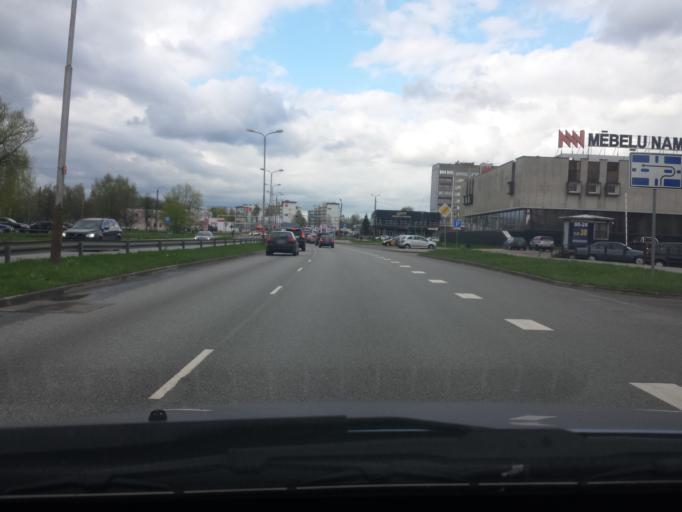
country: LV
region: Riga
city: Riga
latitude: 56.9550
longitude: 24.1888
